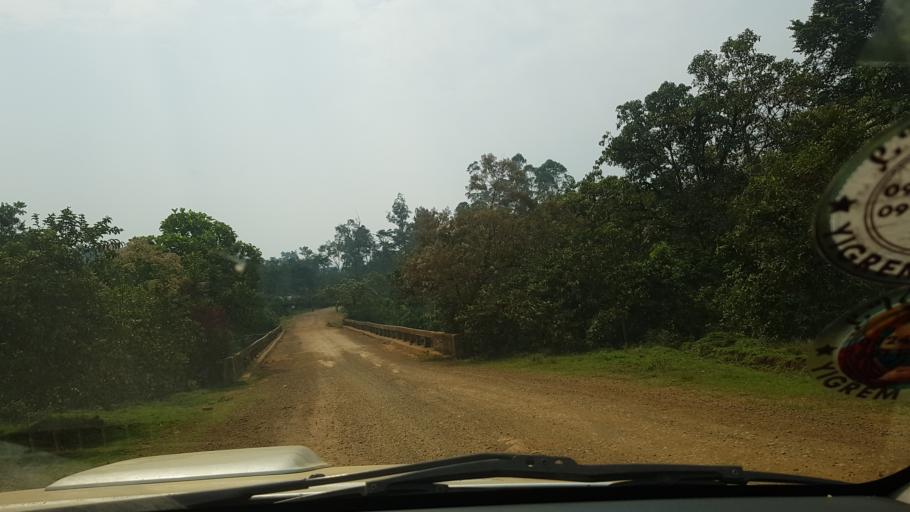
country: ET
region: Oromiya
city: Gore
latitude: 7.8737
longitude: 35.4786
